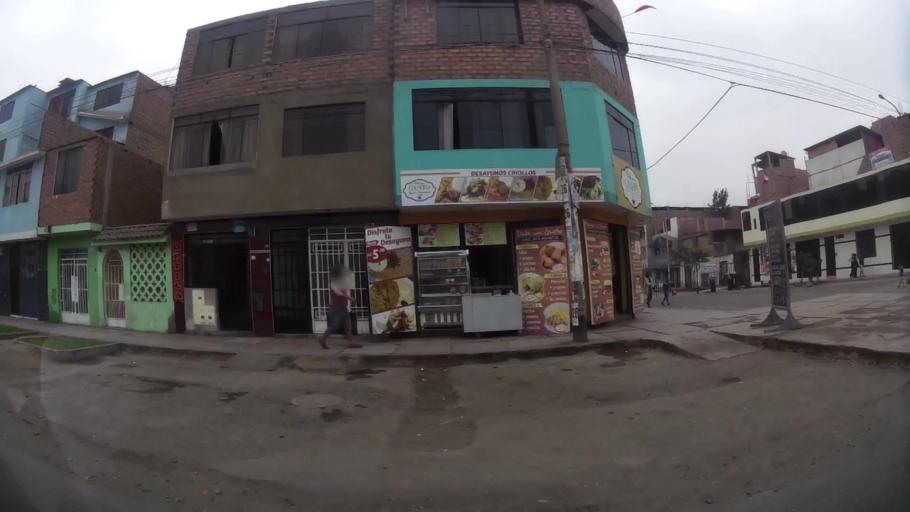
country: PE
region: Lima
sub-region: Lima
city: Independencia
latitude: -11.9492
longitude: -77.0769
